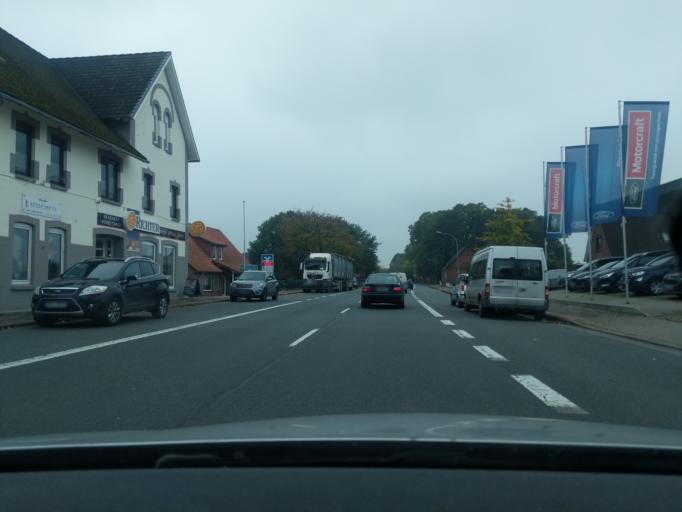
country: DE
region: Lower Saxony
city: Dudenbuttel
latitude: 53.5920
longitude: 9.3543
